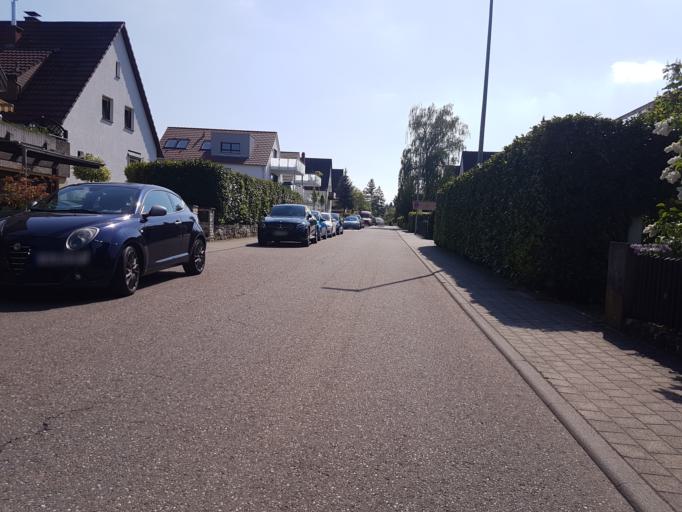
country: DE
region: Baden-Wuerttemberg
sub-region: Regierungsbezirk Stuttgart
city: Bietigheim-Bissingen
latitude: 48.9623
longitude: 9.1370
